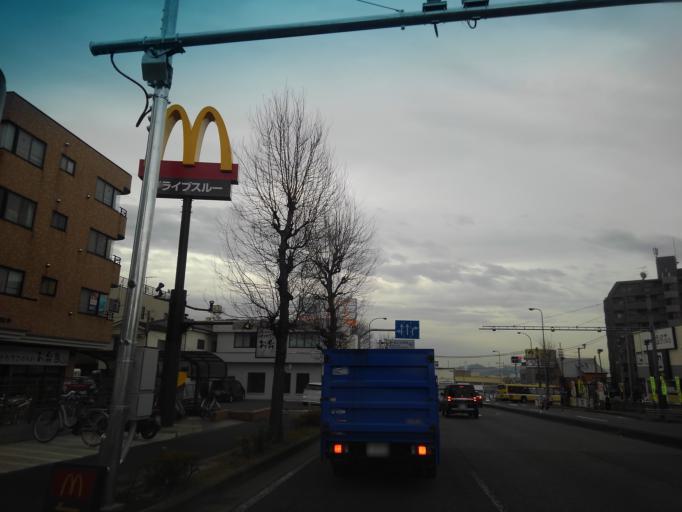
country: JP
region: Tokyo
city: Hachioji
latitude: 35.6670
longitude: 139.3539
